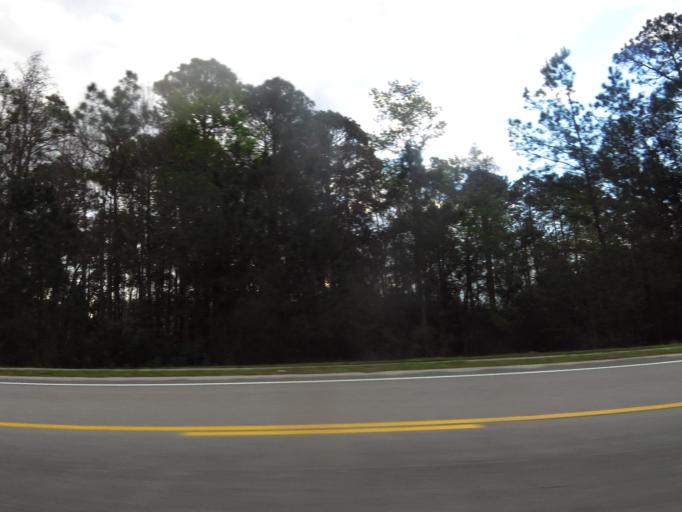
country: US
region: Florida
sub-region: Saint Johns County
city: Fruit Cove
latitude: 30.1815
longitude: -81.5694
